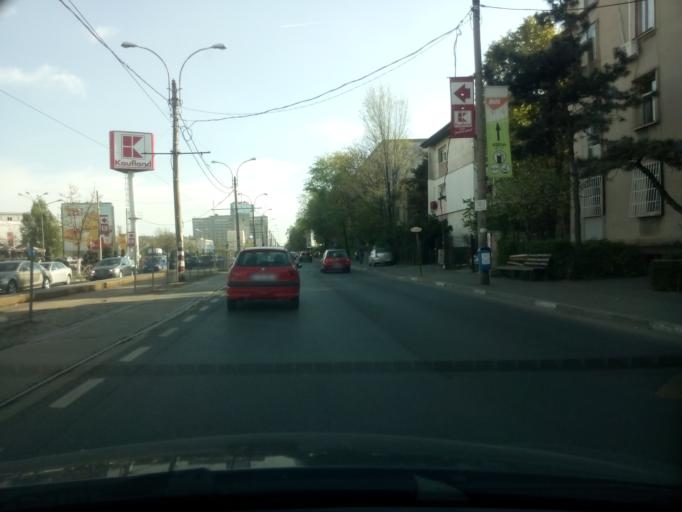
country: RO
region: Bucuresti
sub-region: Municipiul Bucuresti
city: Bucharest
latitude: 44.4645
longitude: 26.1081
